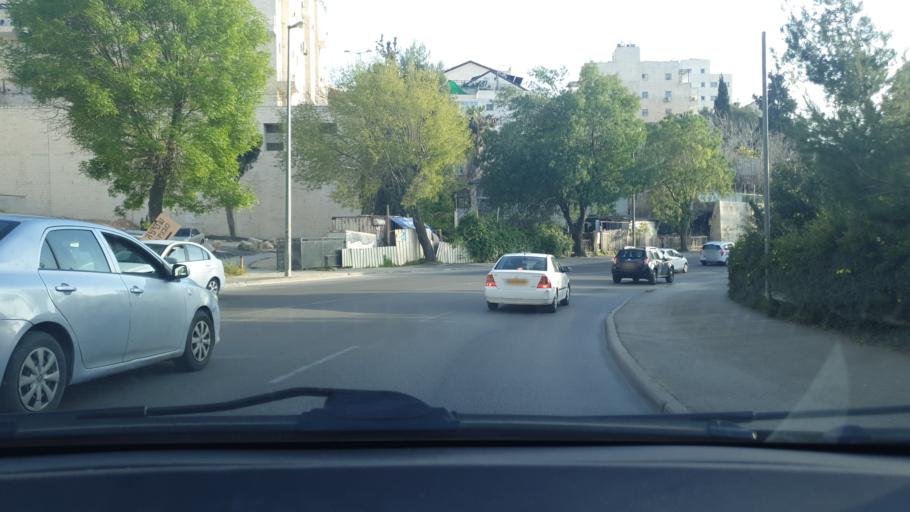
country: PS
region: West Bank
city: Bayt Iksa
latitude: 31.7920
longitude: 35.1902
